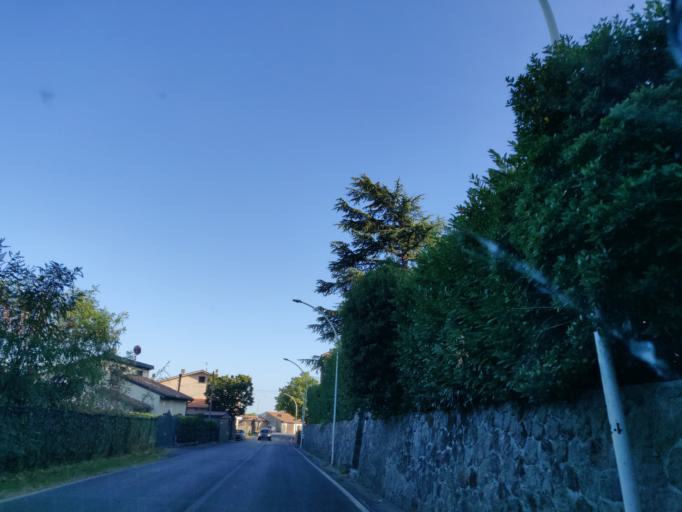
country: IT
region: Tuscany
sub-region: Provincia di Siena
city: Piancastagnaio
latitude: 42.8483
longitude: 11.6953
